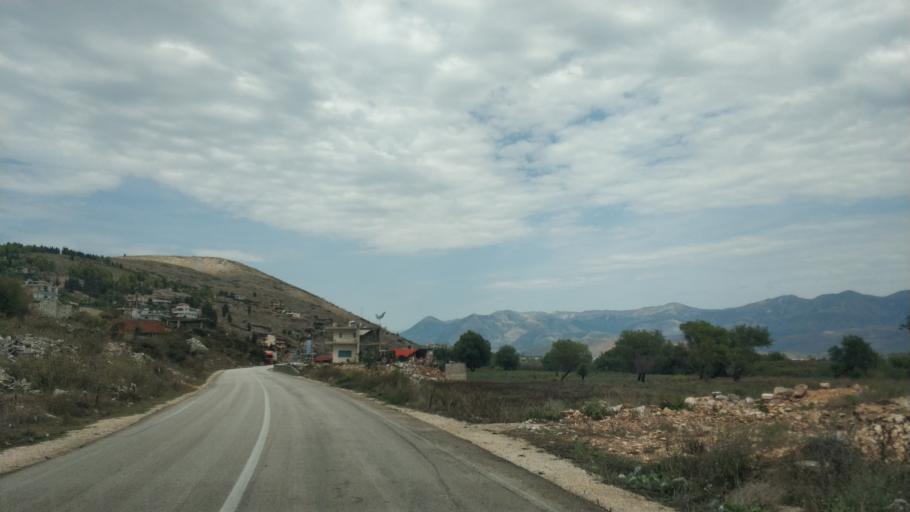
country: AL
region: Vlore
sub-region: Rrethi i Sarandes
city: Sarande
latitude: 39.8470
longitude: 20.0364
